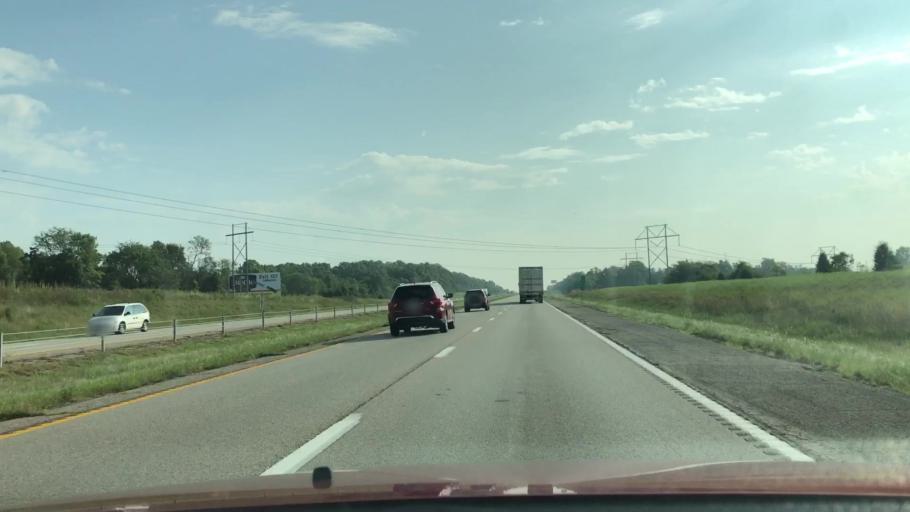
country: US
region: Missouri
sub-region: Laclede County
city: Lebanon
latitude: 37.5803
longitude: -92.7504
